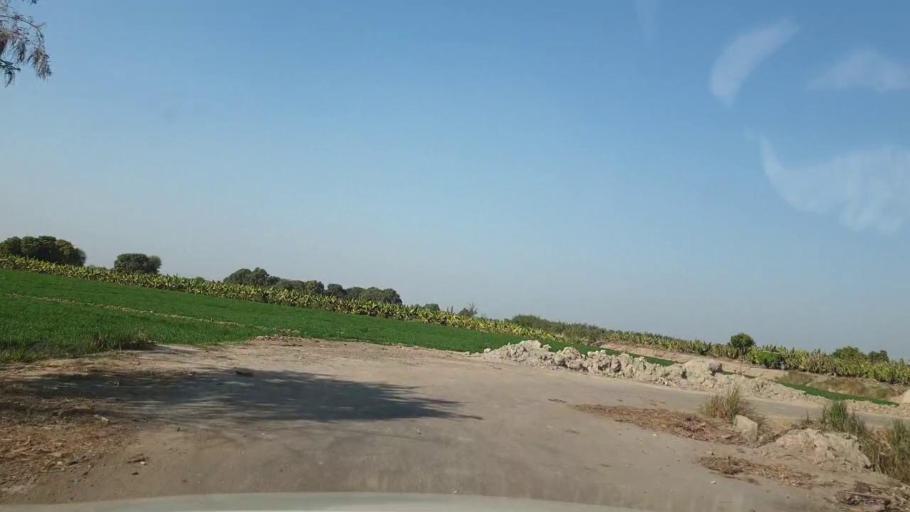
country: PK
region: Sindh
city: Tando Allahyar
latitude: 25.4788
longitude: 68.6598
